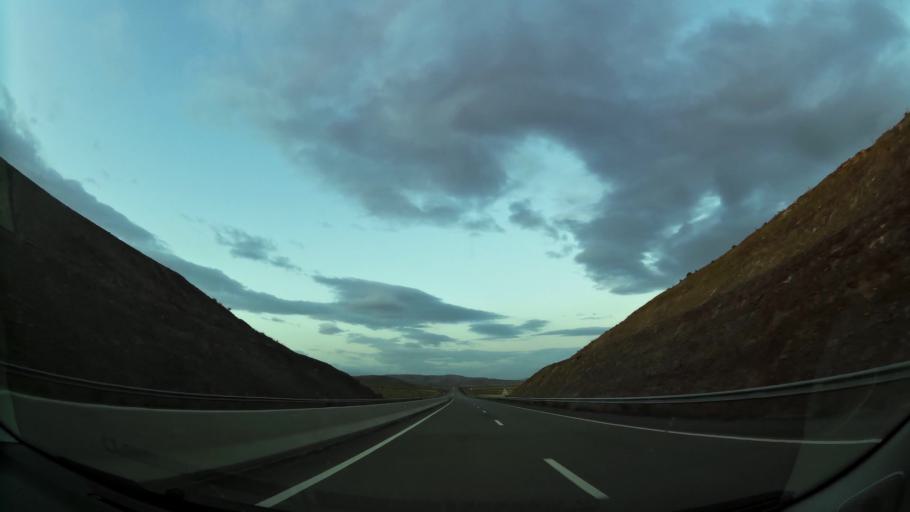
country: MA
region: Oriental
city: El Aioun
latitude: 34.5968
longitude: -2.6467
